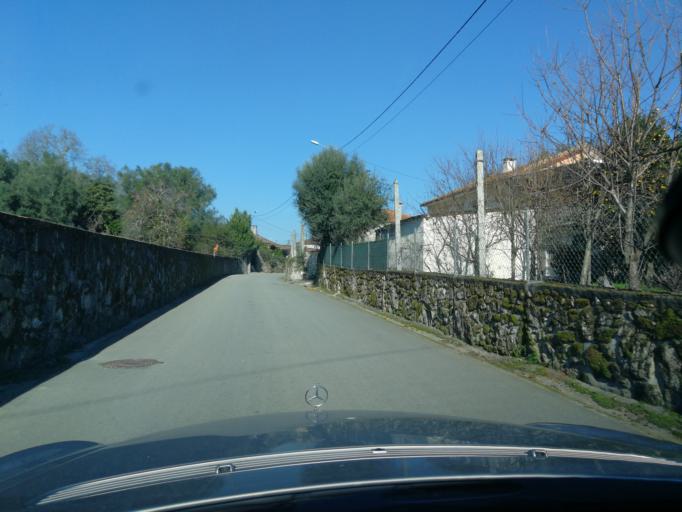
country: PT
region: Braga
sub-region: Braga
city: Adaufe
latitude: 41.6158
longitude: -8.3976
